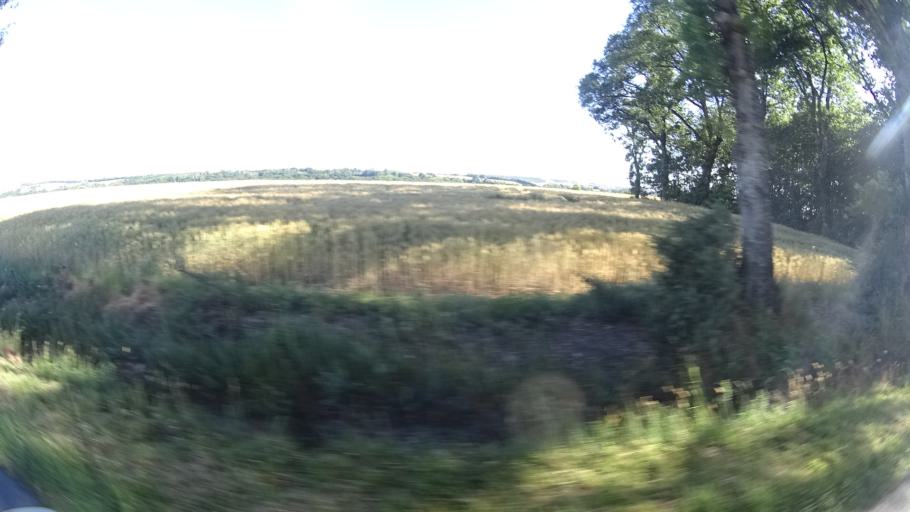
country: FR
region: Brittany
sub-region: Departement d'Ille-et-Vilaine
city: Langon
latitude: 47.7406
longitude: -1.8046
